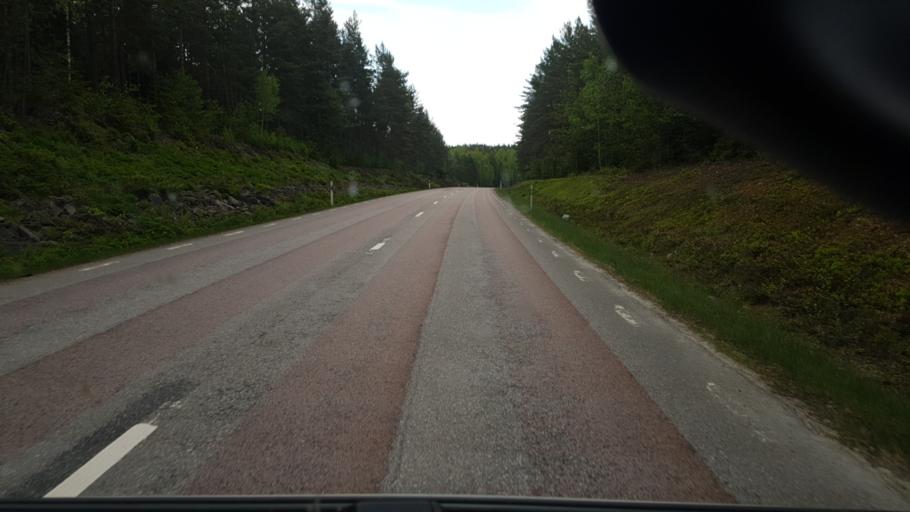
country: SE
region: Vaermland
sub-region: Arvika Kommun
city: Arvika
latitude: 59.5835
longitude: 12.6990
